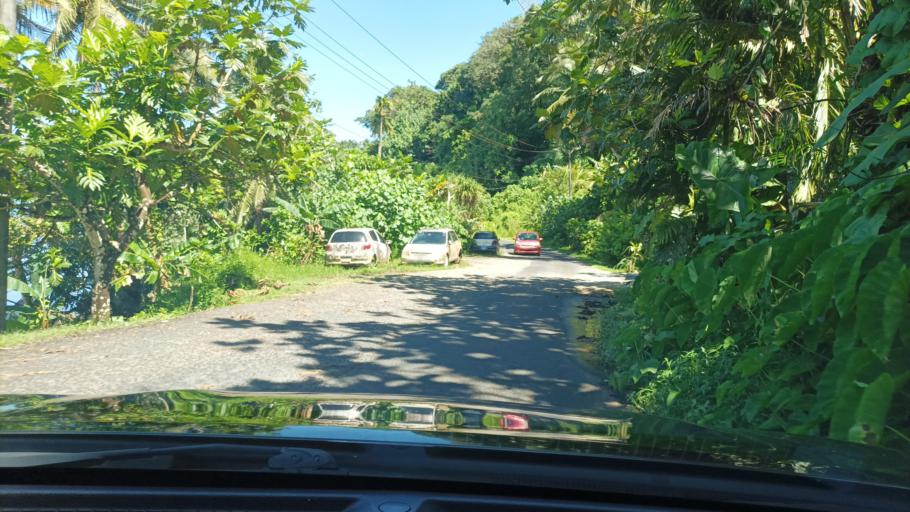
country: FM
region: Pohnpei
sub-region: Madolenihm Municipality
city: Madolenihm Municipality Government
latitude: 6.8563
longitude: 158.2942
